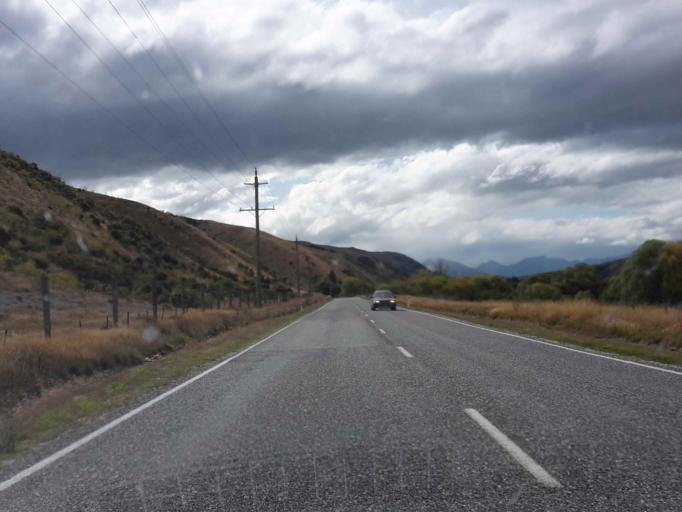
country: NZ
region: Otago
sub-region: Queenstown-Lakes District
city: Wanaka
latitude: -44.8029
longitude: 169.0699
